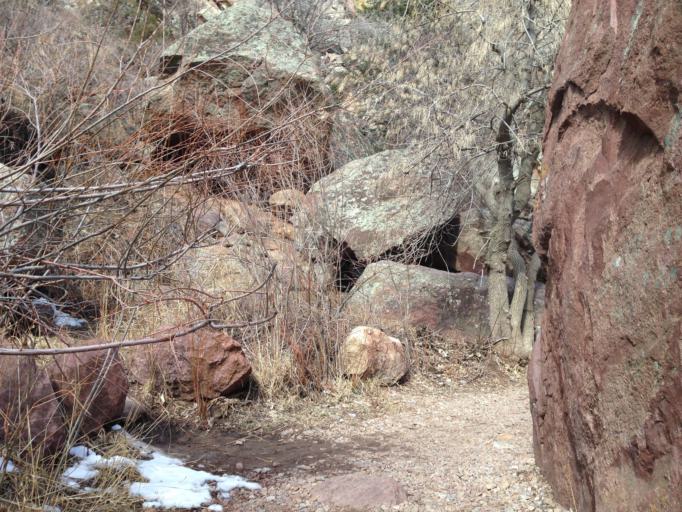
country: US
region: Colorado
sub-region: Boulder County
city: Boulder
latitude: 39.9306
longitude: -105.2840
